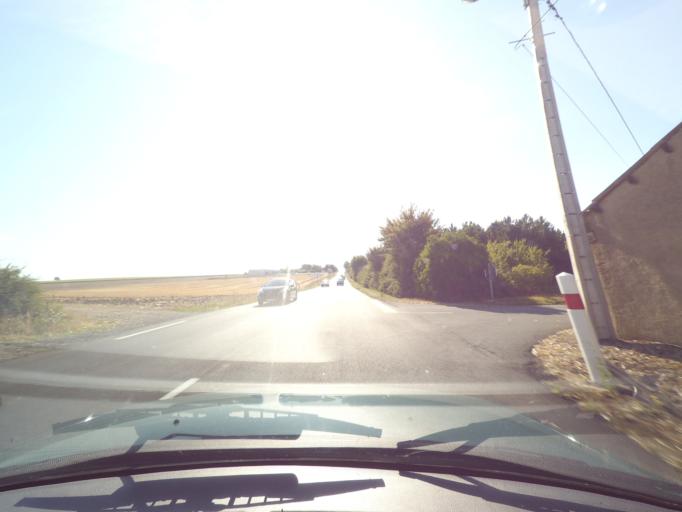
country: FR
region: Poitou-Charentes
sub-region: Departement de la Vienne
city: Vouille
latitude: 46.6476
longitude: 0.1623
